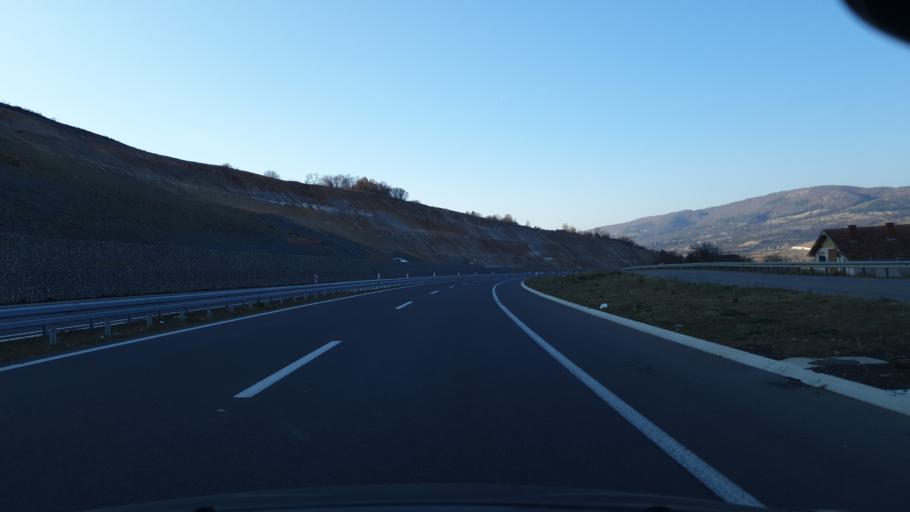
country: RS
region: Central Serbia
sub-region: Pirotski Okrug
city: Dimitrovgrad
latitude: 43.0036
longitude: 22.8069
